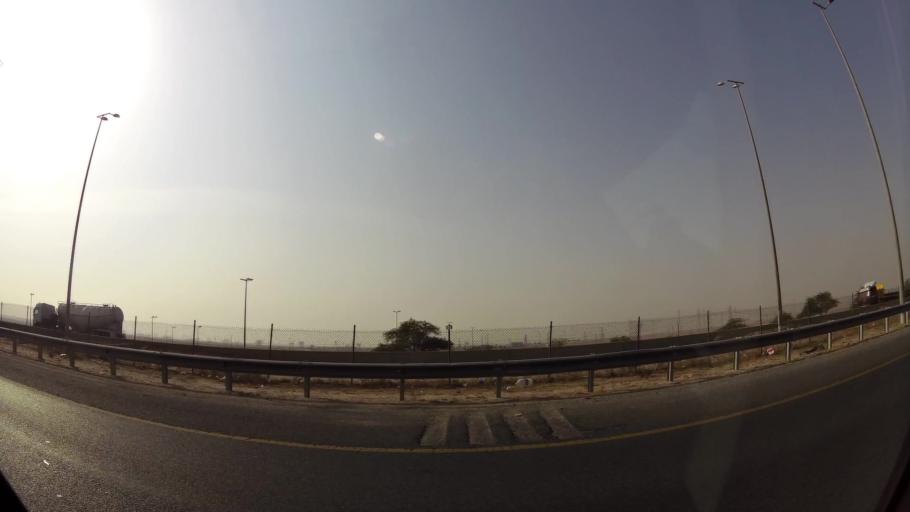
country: KW
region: Al Farwaniyah
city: Janub as Surrah
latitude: 29.1798
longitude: 47.9904
